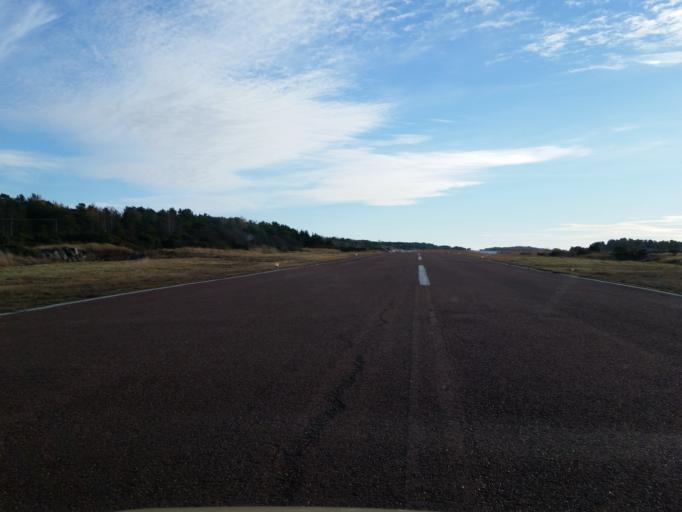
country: AX
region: Alands skaergard
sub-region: Kumlinge
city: Kumlinge
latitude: 60.2445
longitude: 20.8047
